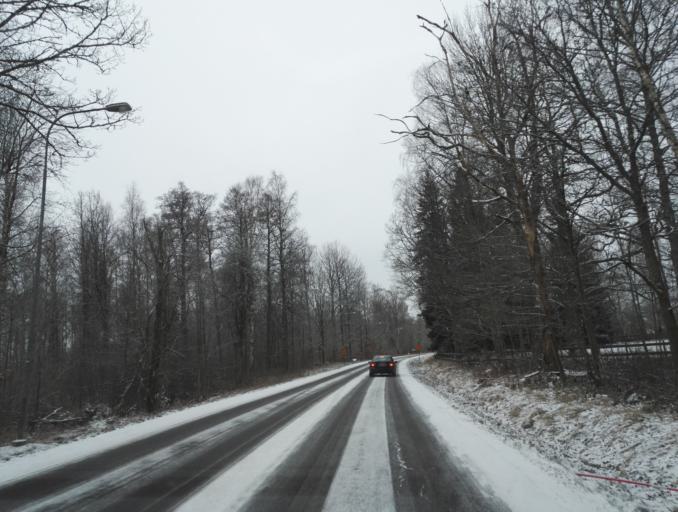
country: SE
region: Kronoberg
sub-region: Lessebo Kommun
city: Lessebo
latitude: 56.7564
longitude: 15.2849
